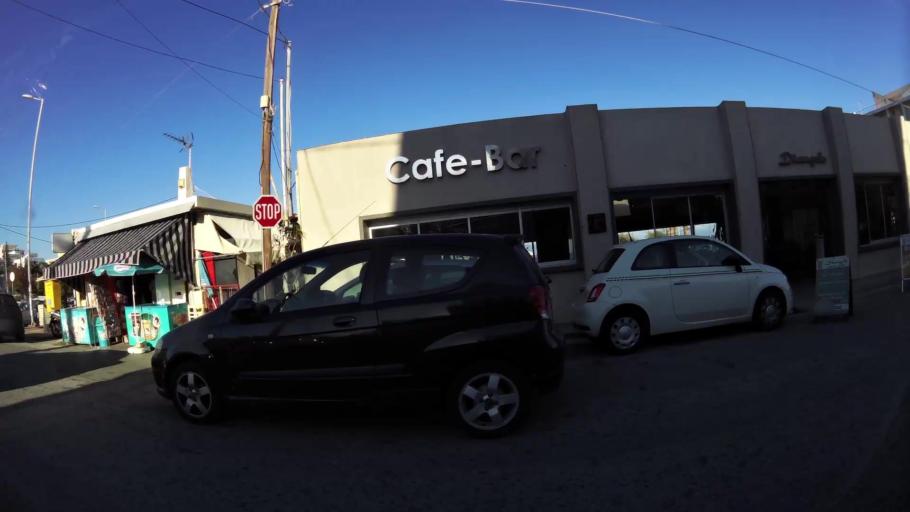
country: GR
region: Attica
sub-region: Nomarchia Anatolikis Attikis
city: Rafina
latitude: 38.0206
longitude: 24.0086
